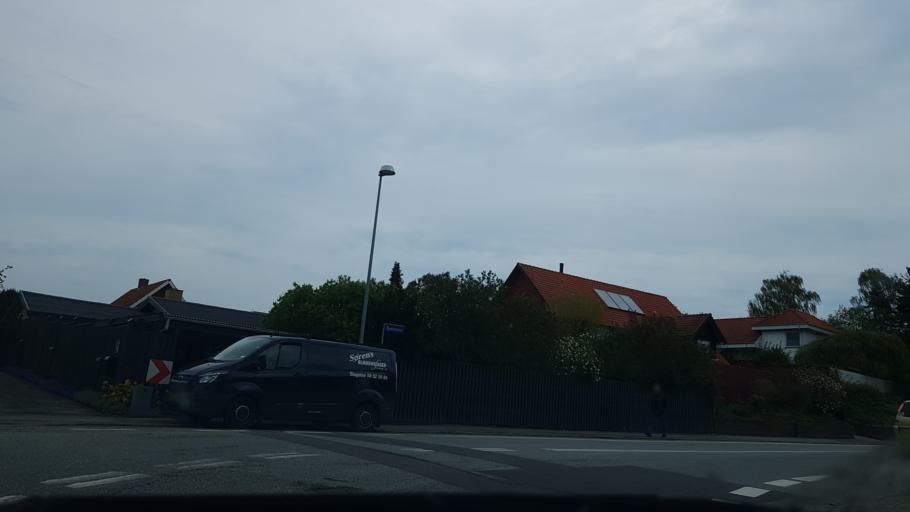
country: DK
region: Zealand
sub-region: Slagelse Kommune
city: Slagelse
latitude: 55.4041
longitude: 11.3812
